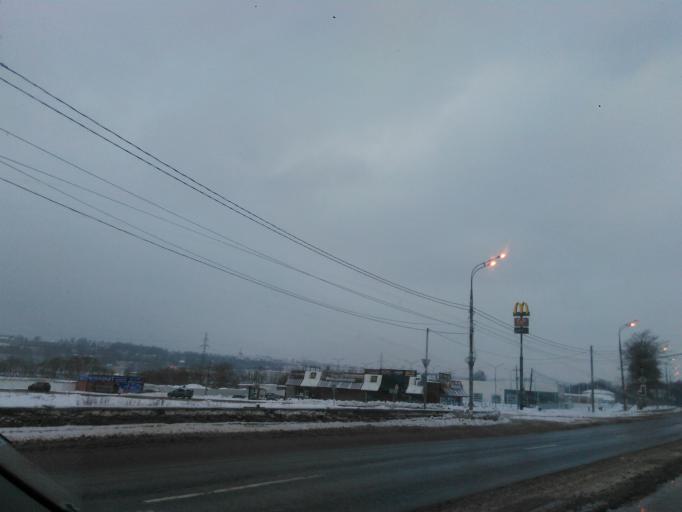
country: RU
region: Moskovskaya
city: Yakhroma
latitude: 56.2793
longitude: 37.5034
